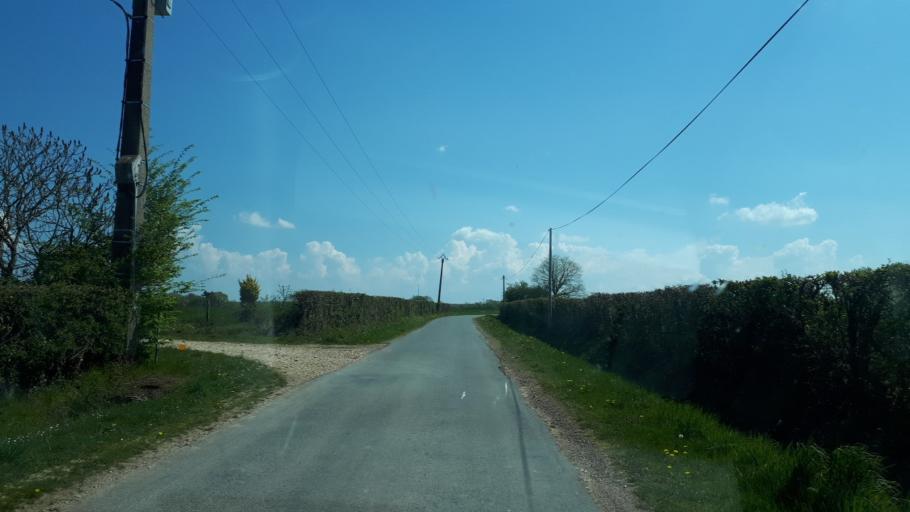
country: FR
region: Centre
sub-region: Departement du Cher
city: Henrichemont
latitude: 47.3057
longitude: 2.5548
